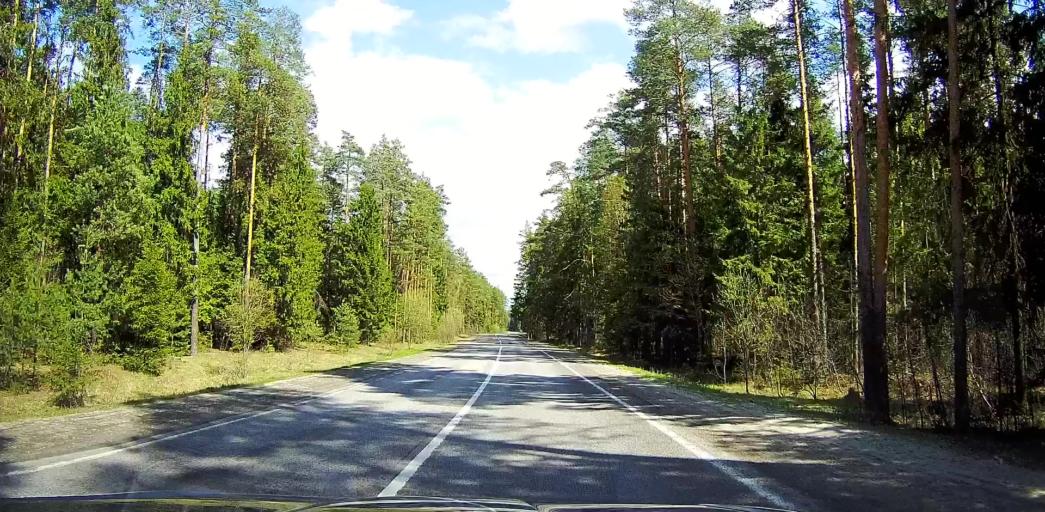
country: RU
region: Moskovskaya
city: Davydovo
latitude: 55.5588
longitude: 38.8393
